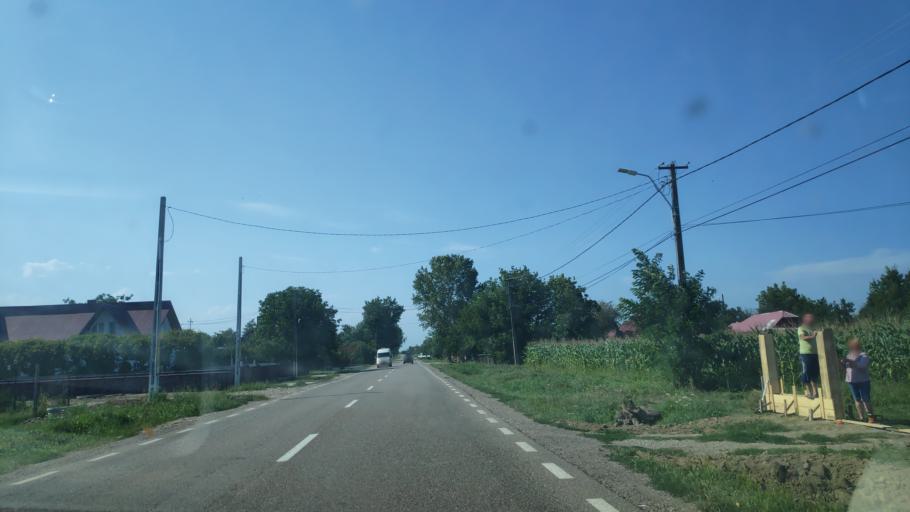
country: RO
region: Suceava
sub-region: Comuna Boroaia
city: Boroaia
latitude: 47.3753
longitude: 26.3236
